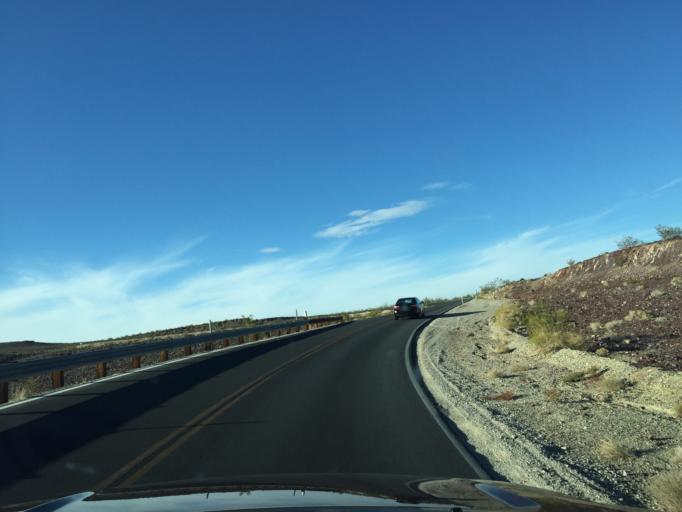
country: US
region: California
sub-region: Inyo County
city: Lone Pine
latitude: 36.3447
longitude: -117.5407
